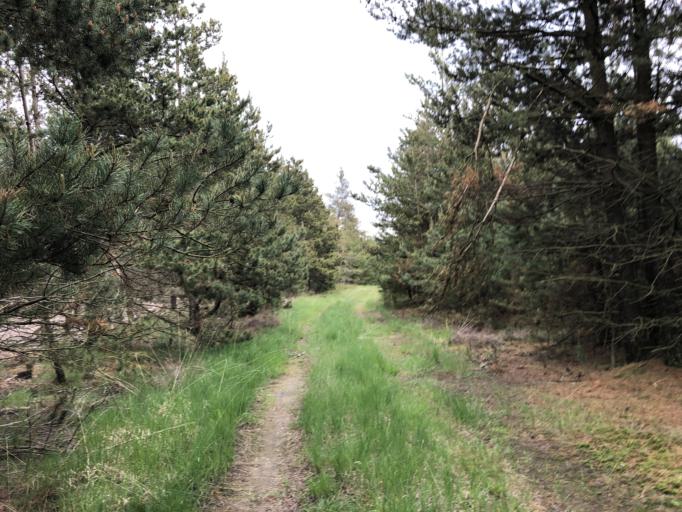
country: DK
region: Central Jutland
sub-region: Holstebro Kommune
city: Ulfborg
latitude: 56.2767
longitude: 8.3626
